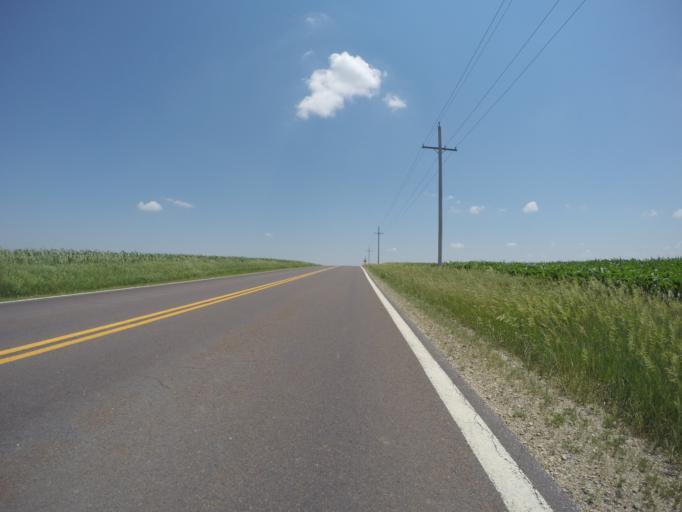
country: US
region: Kansas
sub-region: Doniphan County
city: Troy
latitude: 39.7400
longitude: -95.1491
